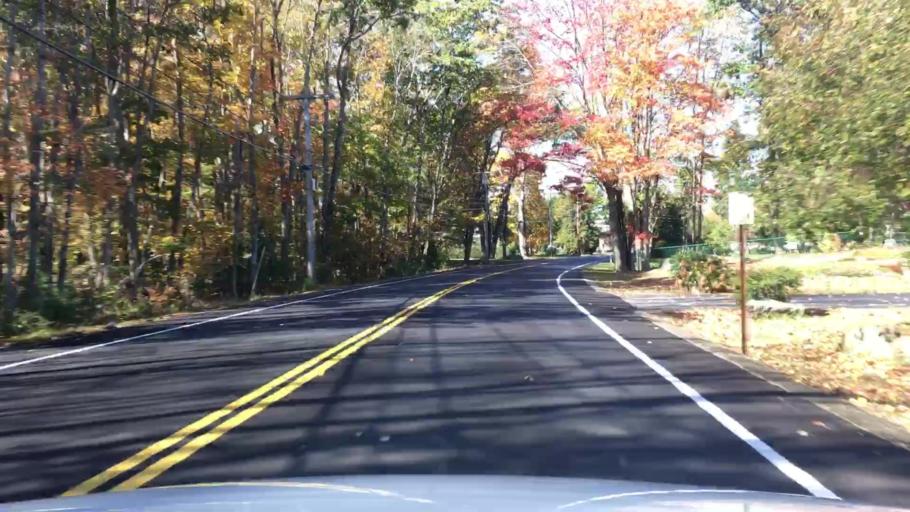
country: US
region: Maine
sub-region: York County
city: Biddeford
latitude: 43.4632
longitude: -70.4383
